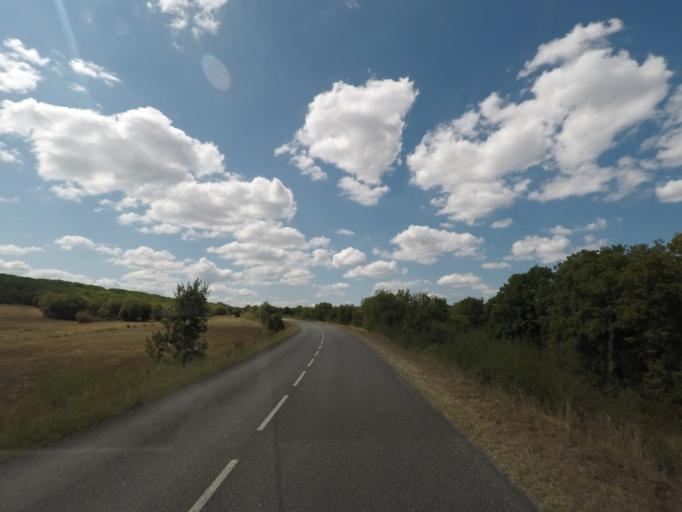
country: FR
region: Midi-Pyrenees
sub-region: Departement du Lot
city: Cajarc
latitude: 44.5860
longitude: 1.7155
